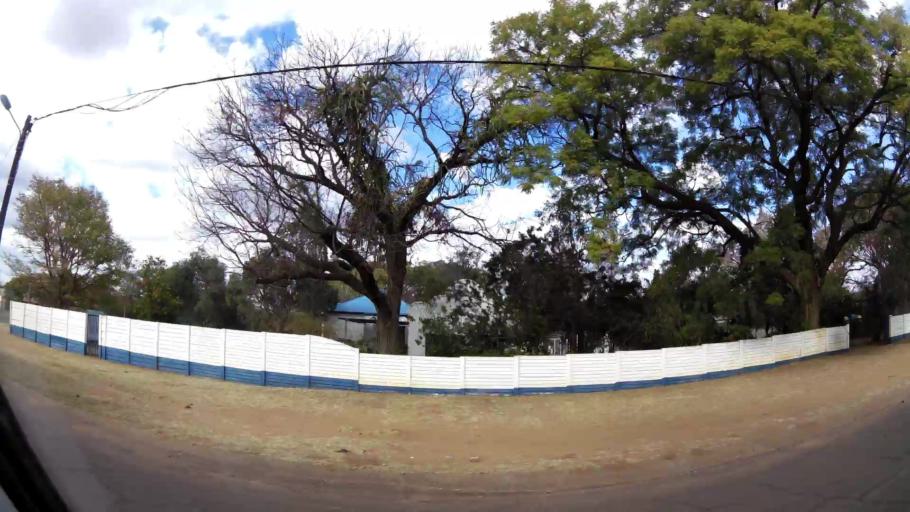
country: ZA
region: Limpopo
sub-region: Waterberg District Municipality
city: Modimolle
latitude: -24.7048
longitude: 28.4059
